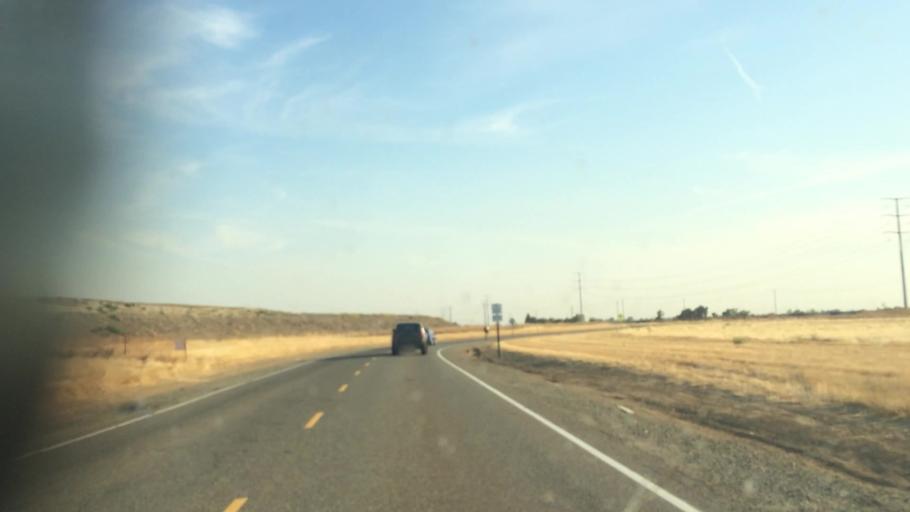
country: US
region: California
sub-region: Sacramento County
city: Laguna
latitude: 38.4382
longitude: -121.4598
